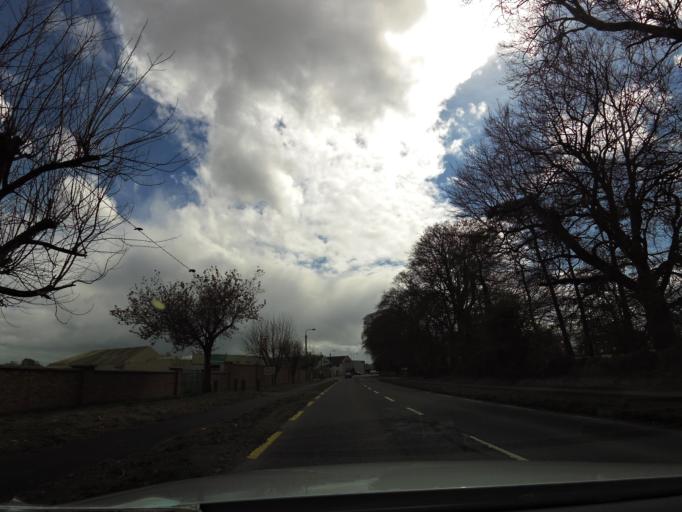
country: IE
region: Munster
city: Thurles
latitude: 52.6855
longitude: -7.8134
